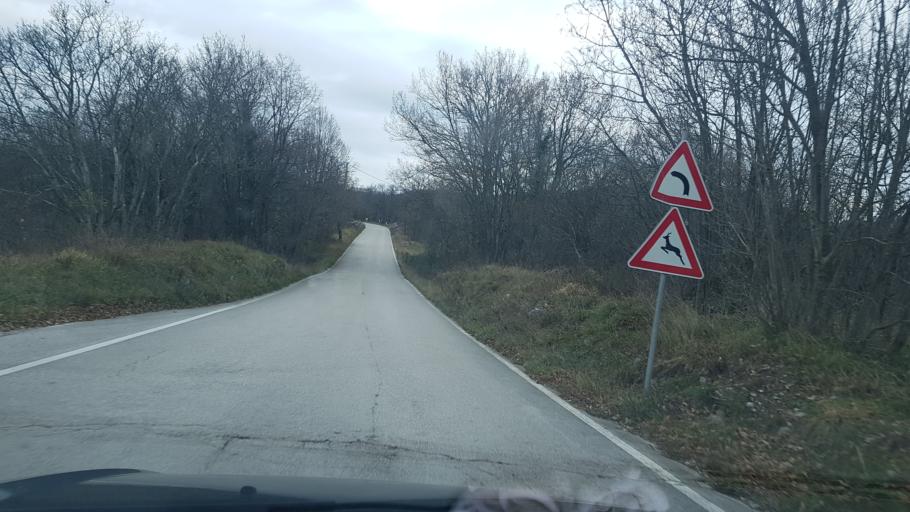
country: IT
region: Friuli Venezia Giulia
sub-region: Provincia di Trieste
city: Zolla
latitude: 45.7022
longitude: 13.8286
